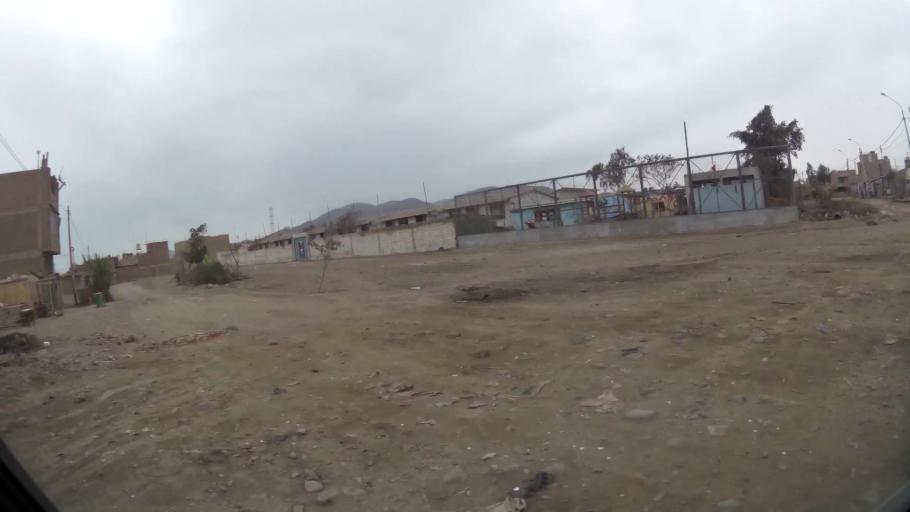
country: PE
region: Lima
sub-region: Lima
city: Independencia
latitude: -11.9579
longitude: -77.1009
